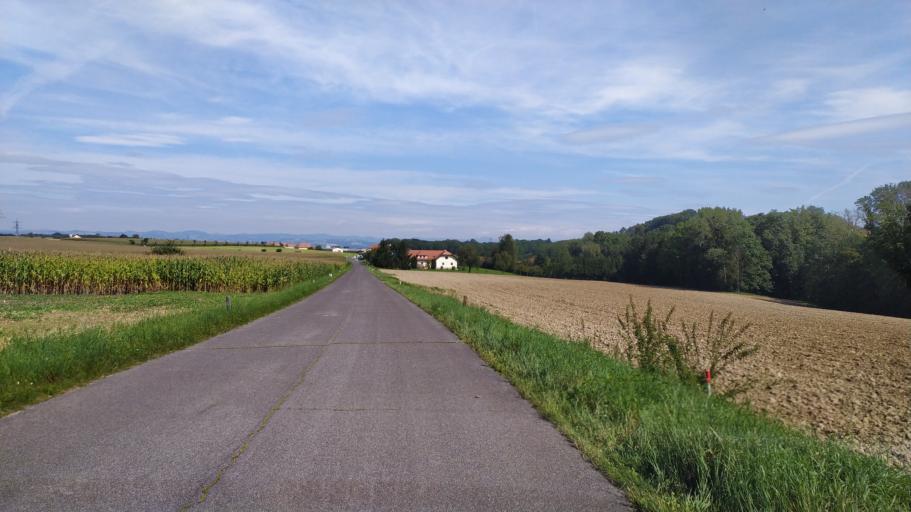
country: AT
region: Lower Austria
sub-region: Politischer Bezirk Amstetten
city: Strengberg
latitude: 48.1463
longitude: 14.6215
